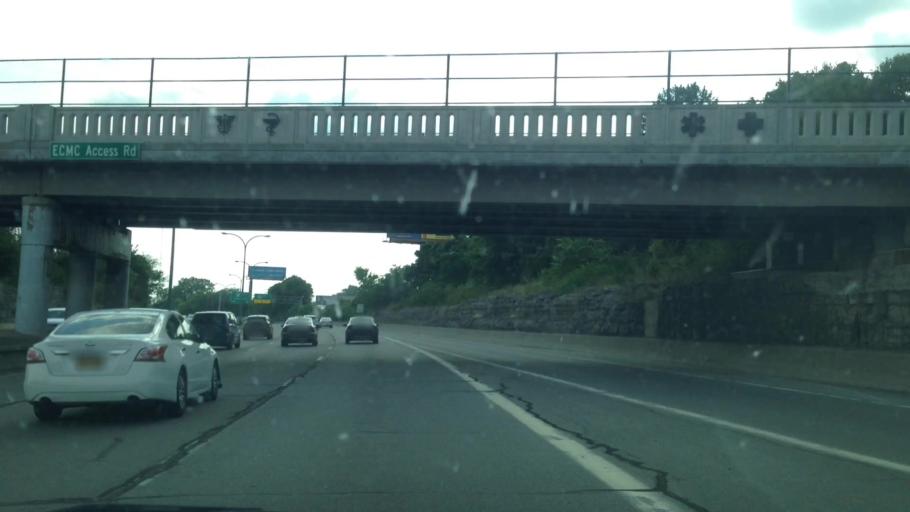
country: US
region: New York
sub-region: Erie County
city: Eggertsville
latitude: 42.9296
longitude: -78.8322
